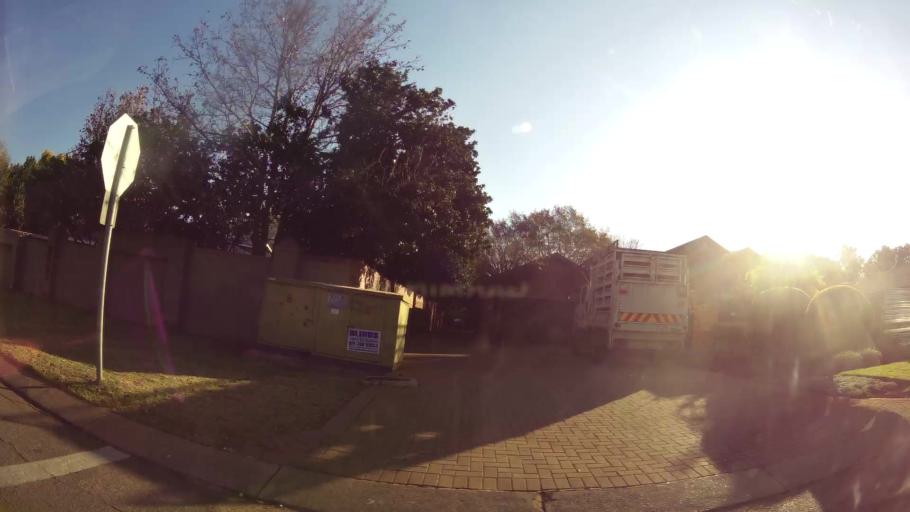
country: ZA
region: Gauteng
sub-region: City of Tshwane Metropolitan Municipality
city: Centurion
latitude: -25.8549
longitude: 28.1576
